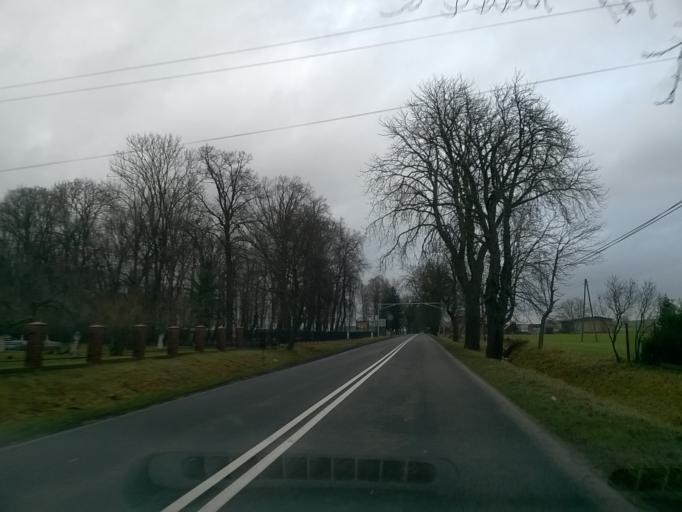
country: PL
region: Kujawsko-Pomorskie
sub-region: Powiat nakielski
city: Kcynia
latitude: 52.9823
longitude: 17.4651
